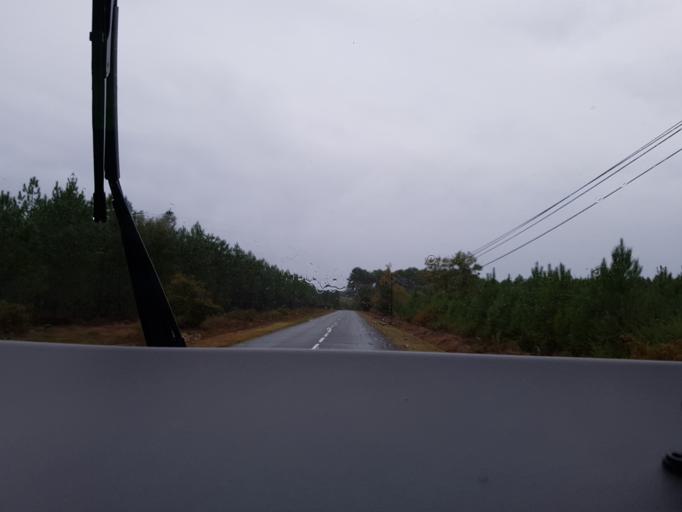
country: FR
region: Aquitaine
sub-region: Departement de la Gironde
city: Saint-Symphorien
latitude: 44.3570
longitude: -0.6295
